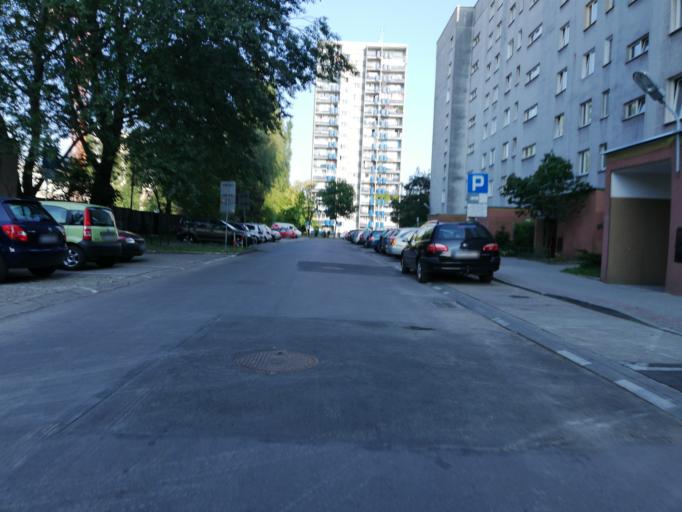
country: PL
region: Lesser Poland Voivodeship
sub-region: Krakow
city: Krakow
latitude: 50.0785
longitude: 20.0073
